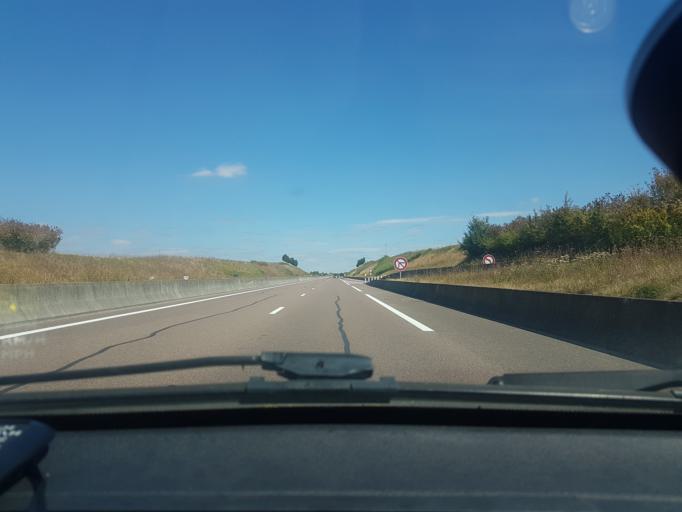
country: FR
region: Bourgogne
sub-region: Departement de la Cote-d'Or
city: Varois-et-Chaignot
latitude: 47.3399
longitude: 5.1323
